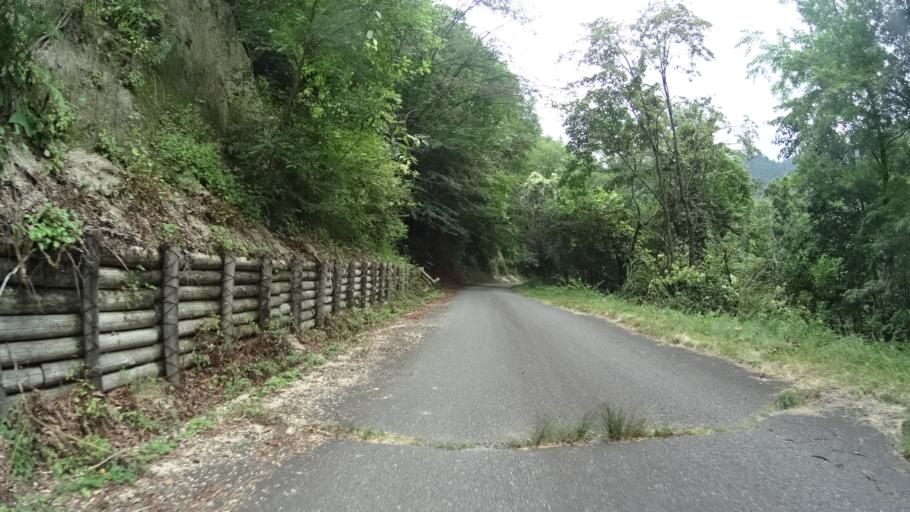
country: JP
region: Yamanashi
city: Kofu-shi
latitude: 35.8247
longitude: 138.5958
